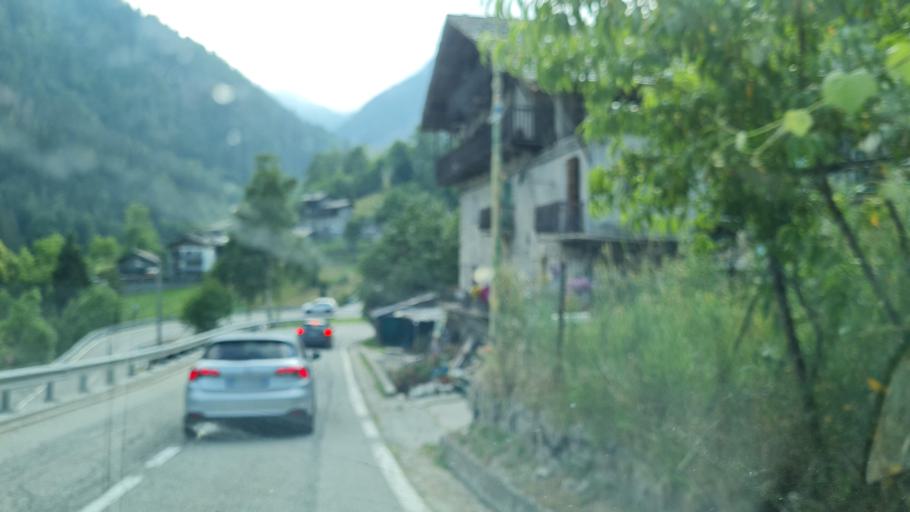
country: IT
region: Aosta Valley
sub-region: Valle d'Aosta
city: Pont-Bozet
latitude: 45.6215
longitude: 7.6560
